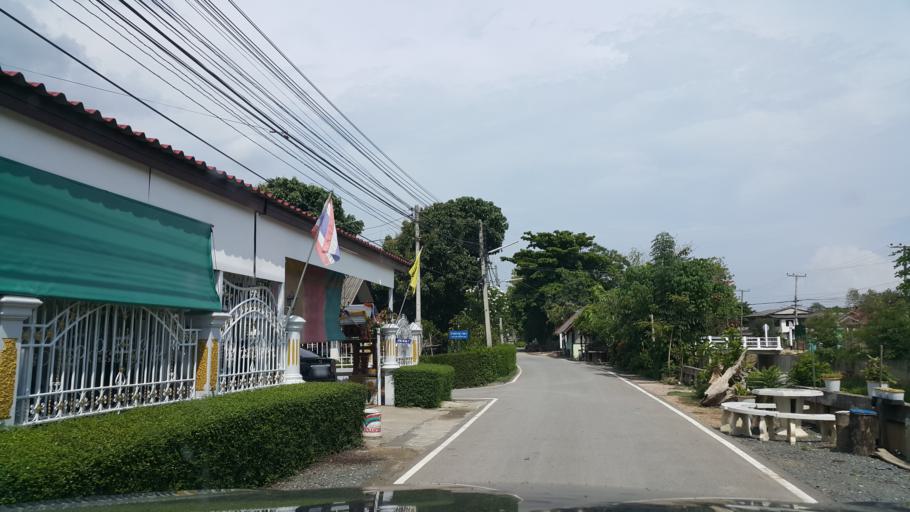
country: TH
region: Chiang Mai
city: San Kamphaeng
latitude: 18.7337
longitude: 99.1227
